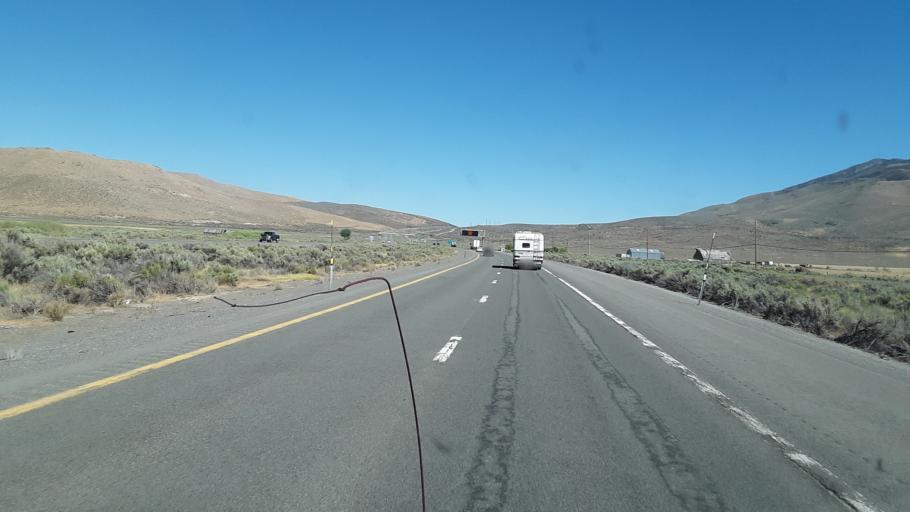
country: US
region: Nevada
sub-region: Washoe County
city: Cold Springs
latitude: 39.6513
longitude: -119.9794
